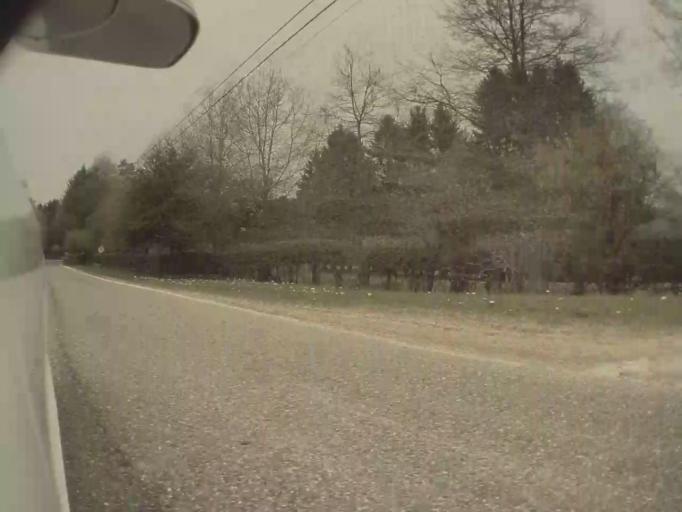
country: BE
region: Wallonia
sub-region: Province du Luxembourg
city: La Roche-en-Ardenne
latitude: 50.2303
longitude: 5.6245
